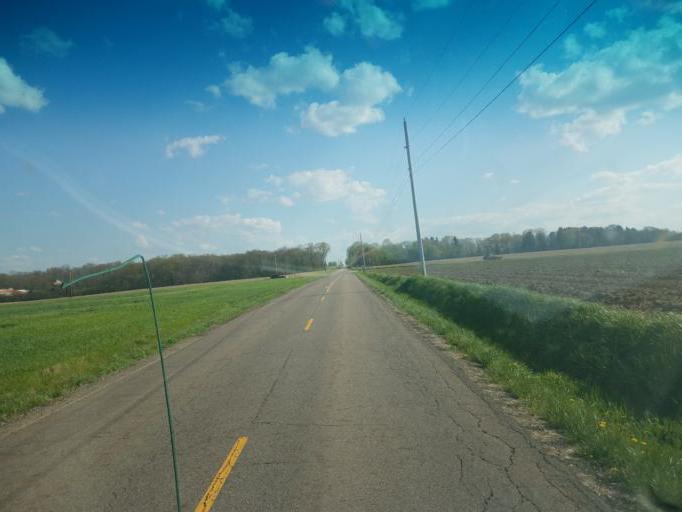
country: US
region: Ohio
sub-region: Wayne County
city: Smithville
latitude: 40.8670
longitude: -81.8781
